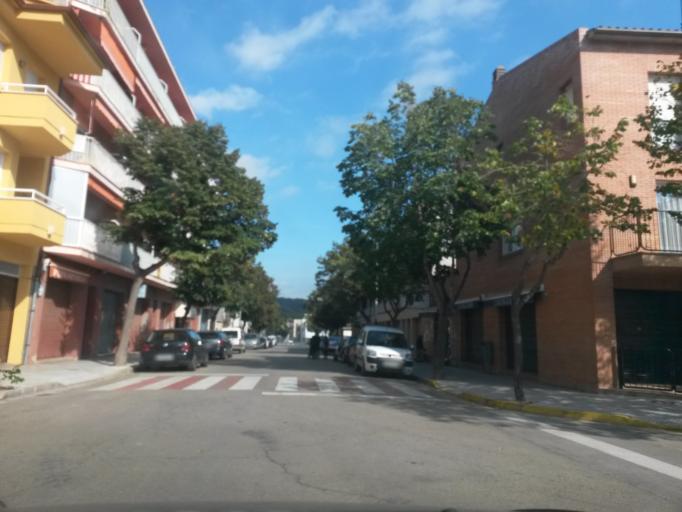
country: ES
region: Catalonia
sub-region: Provincia de Girona
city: Bescano
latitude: 41.9646
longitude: 2.7386
